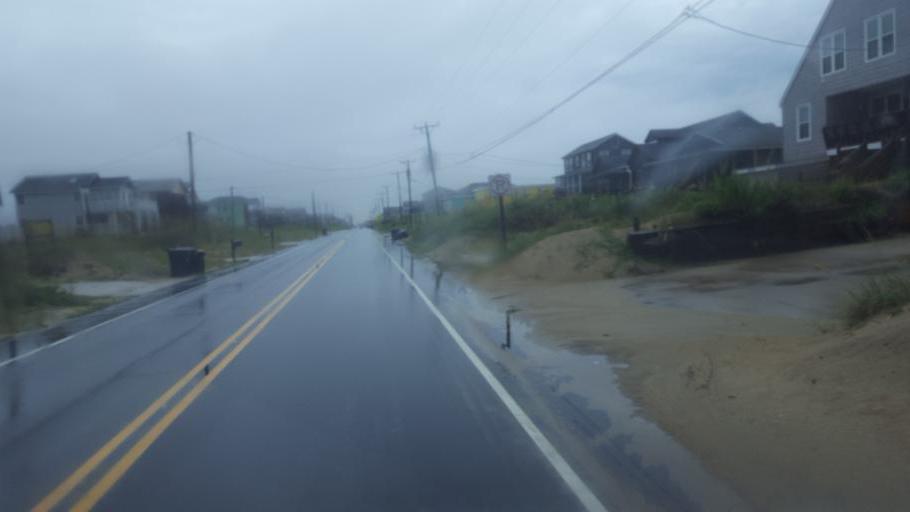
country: US
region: North Carolina
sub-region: Dare County
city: Kill Devil Hills
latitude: 36.0468
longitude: -75.6771
